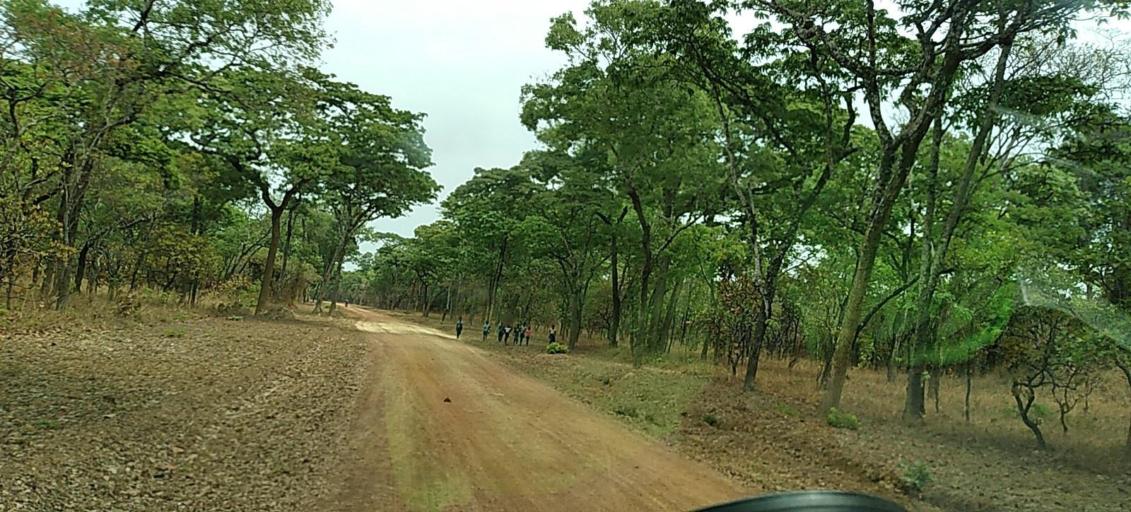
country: ZM
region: North-Western
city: Solwezi
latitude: -12.9473
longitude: 26.5596
